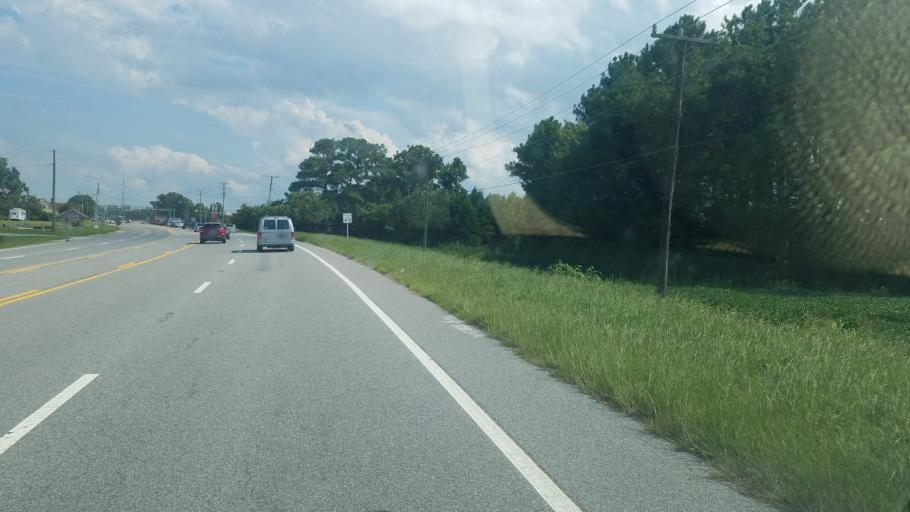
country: US
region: North Carolina
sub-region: Currituck County
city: Currituck
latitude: 36.3887
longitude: -75.9784
